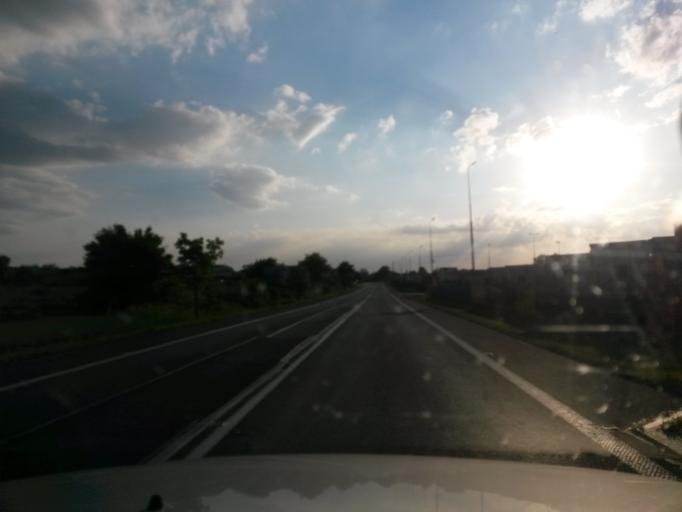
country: PL
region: Lodz Voivodeship
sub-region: Powiat wielunski
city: Wielun
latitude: 51.2295
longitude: 18.6131
